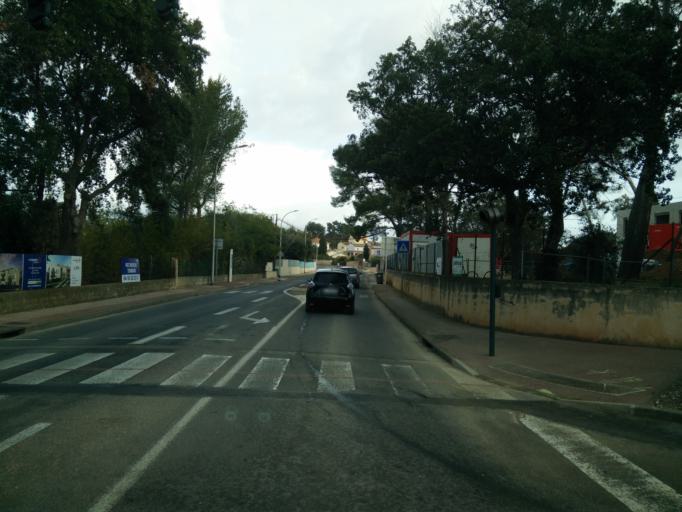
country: FR
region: Provence-Alpes-Cote d'Azur
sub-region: Departement du Var
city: Six-Fours-les-Plages
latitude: 43.0839
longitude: 5.8223
